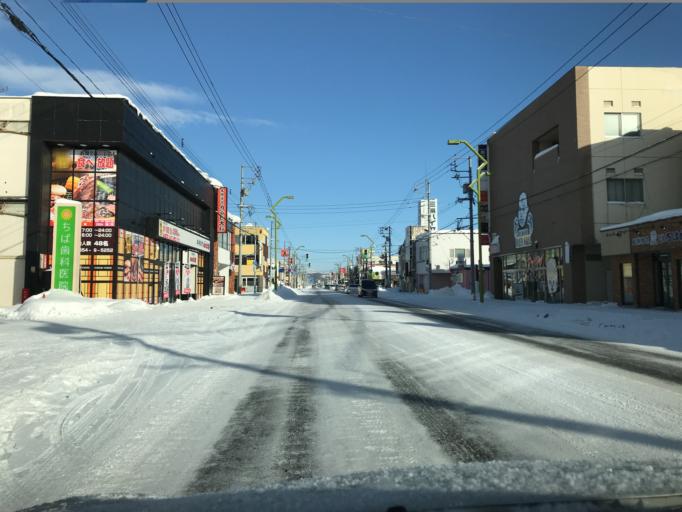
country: JP
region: Hokkaido
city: Nayoro
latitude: 44.3507
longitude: 142.4571
